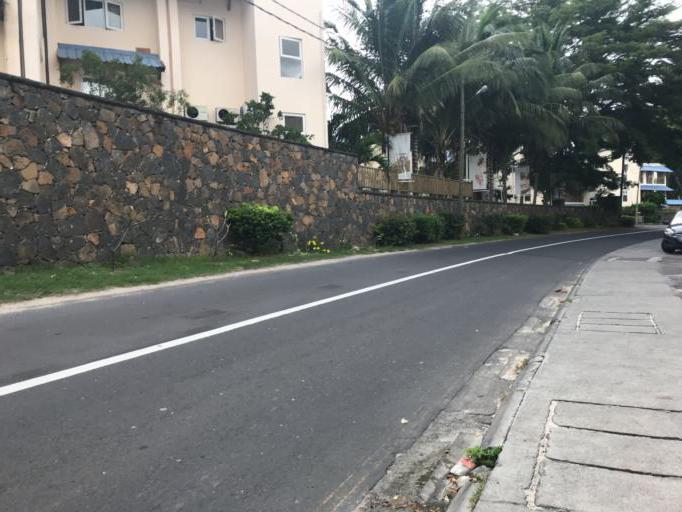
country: MU
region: Black River
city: Flic en Flac
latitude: -20.2939
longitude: 57.3641
